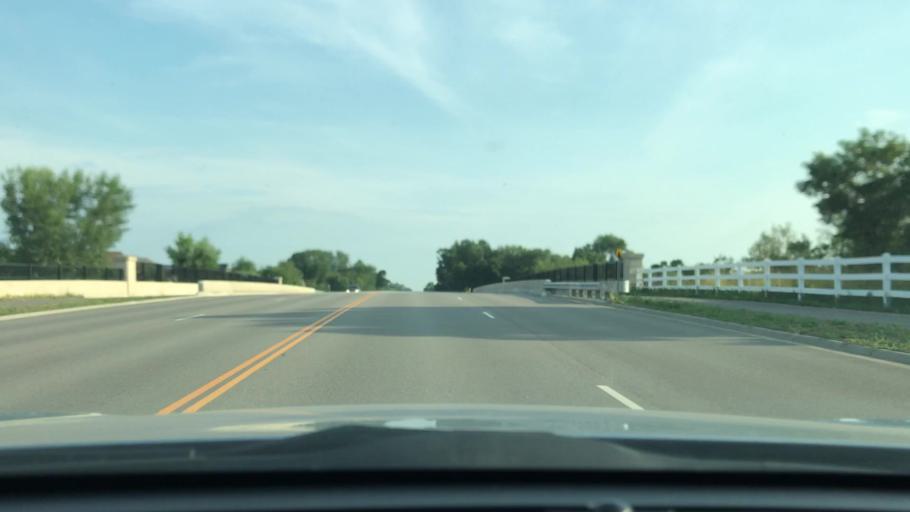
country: US
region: Minnesota
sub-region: Hennepin County
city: Maple Grove
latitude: 45.0506
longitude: -93.4818
